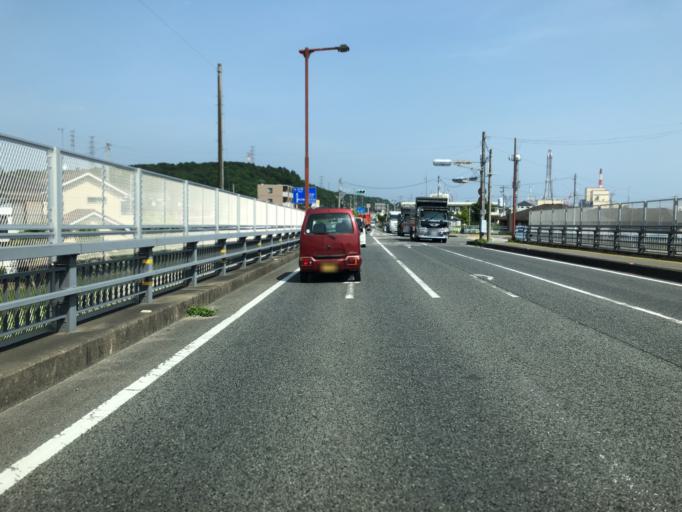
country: JP
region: Ibaraki
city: Kitaibaraki
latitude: 36.9246
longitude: 140.7970
